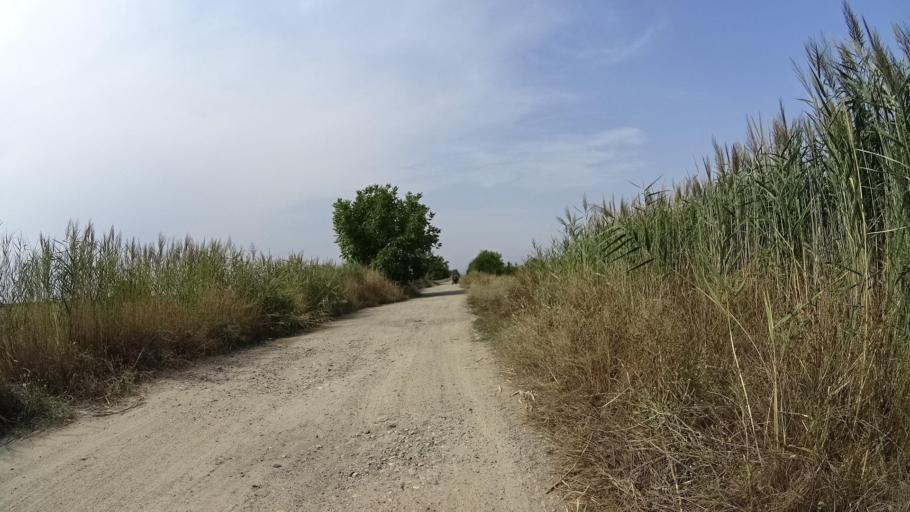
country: BG
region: Plovdiv
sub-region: Obshtina Kaloyanovo
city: Kaloyanovo
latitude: 42.2759
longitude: 24.8004
